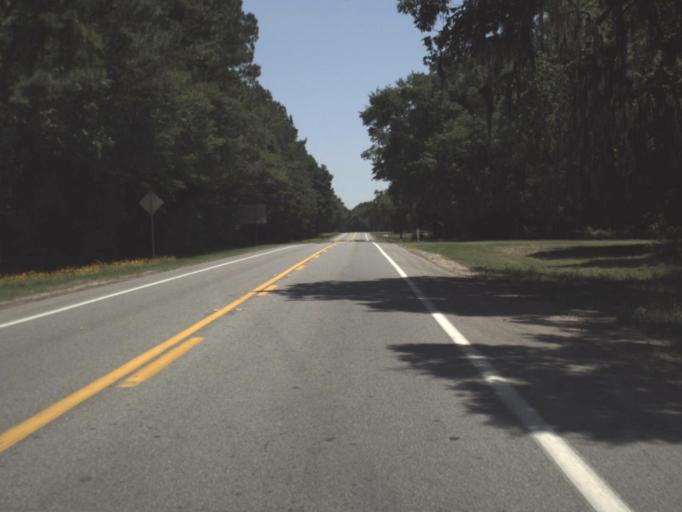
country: US
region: Florida
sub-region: Suwannee County
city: Live Oak
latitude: 30.3752
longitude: -83.1610
